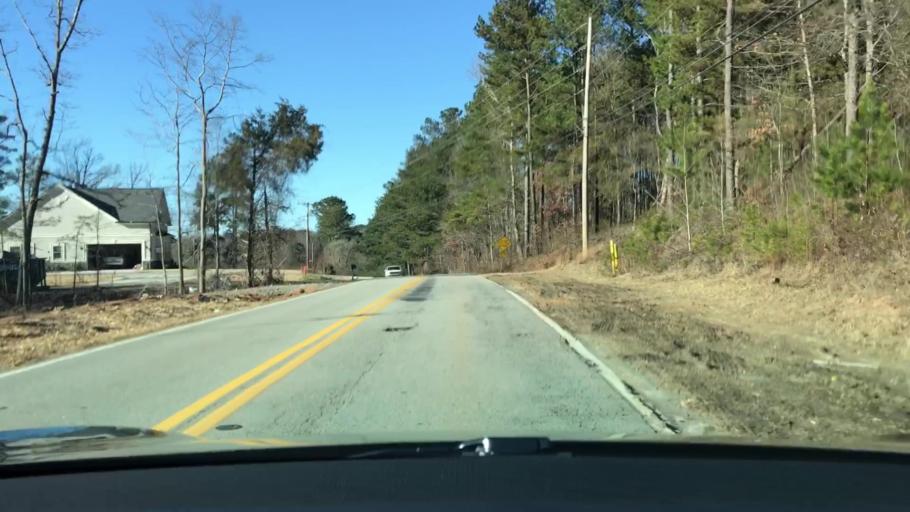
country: US
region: Georgia
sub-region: Barrow County
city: Auburn
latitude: 34.0464
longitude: -83.8450
